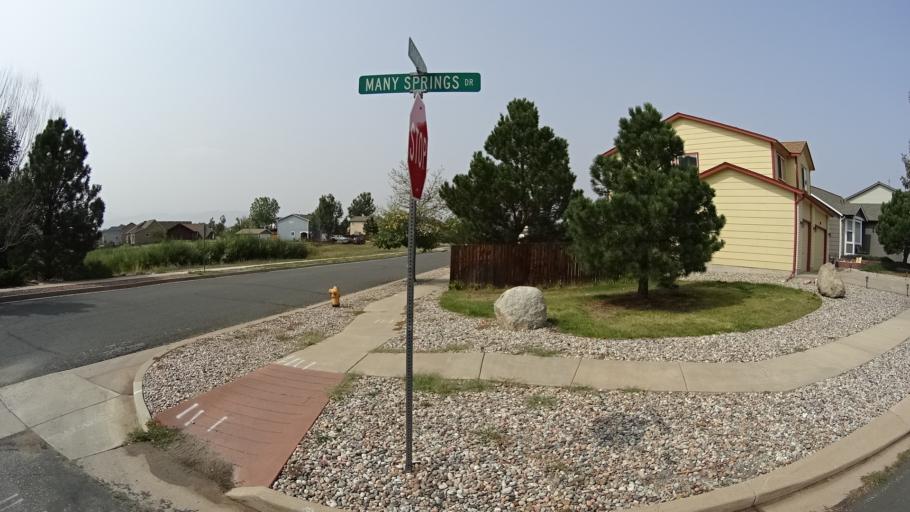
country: US
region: Colorado
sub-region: El Paso County
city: Cimarron Hills
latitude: 38.9256
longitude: -104.7267
